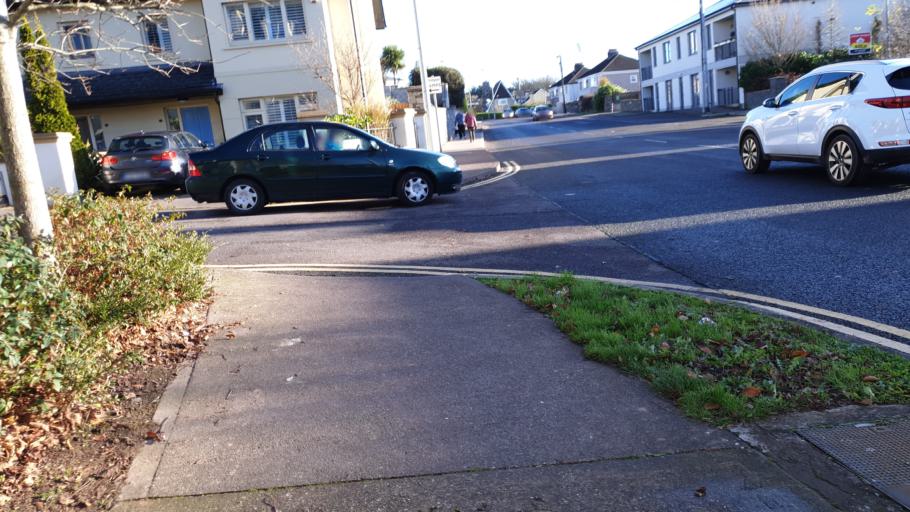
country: IE
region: Munster
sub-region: County Cork
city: Cork
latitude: 51.8913
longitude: -8.4439
